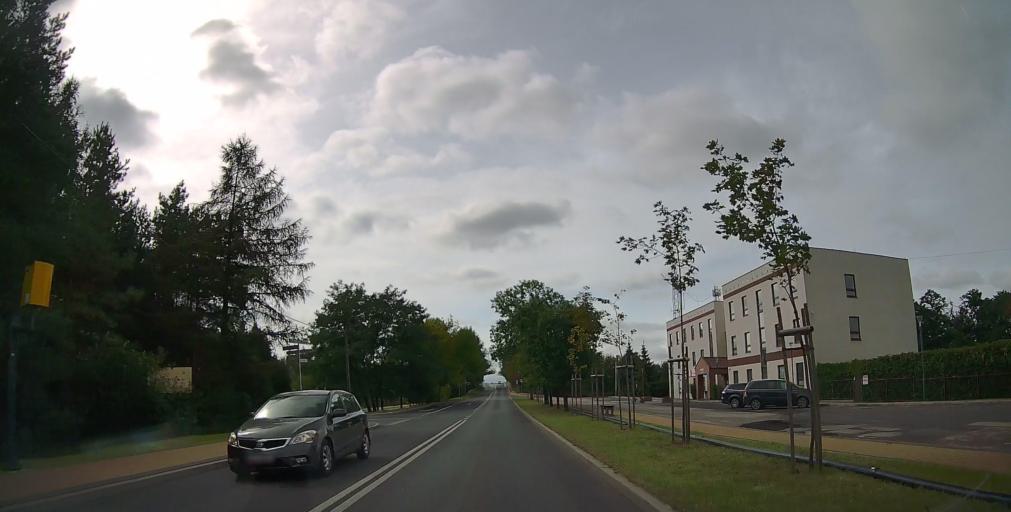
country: PL
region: Masovian Voivodeship
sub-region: Powiat grojecki
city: Grojec
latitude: 51.8638
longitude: 20.8588
